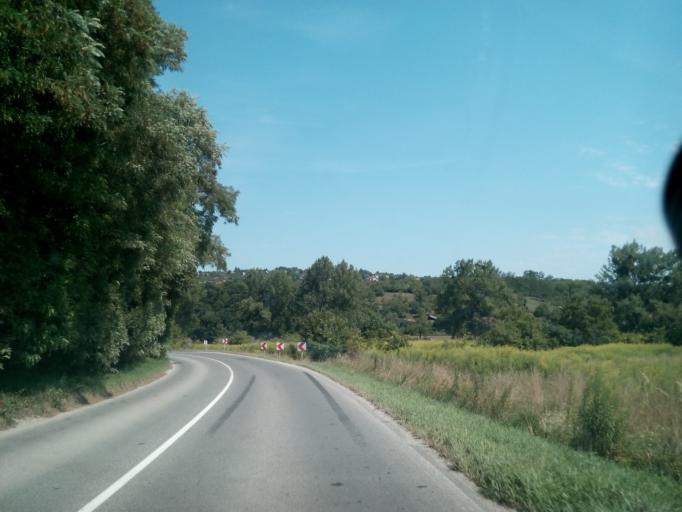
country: SK
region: Kosicky
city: Kosice
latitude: 48.7572
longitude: 21.2484
